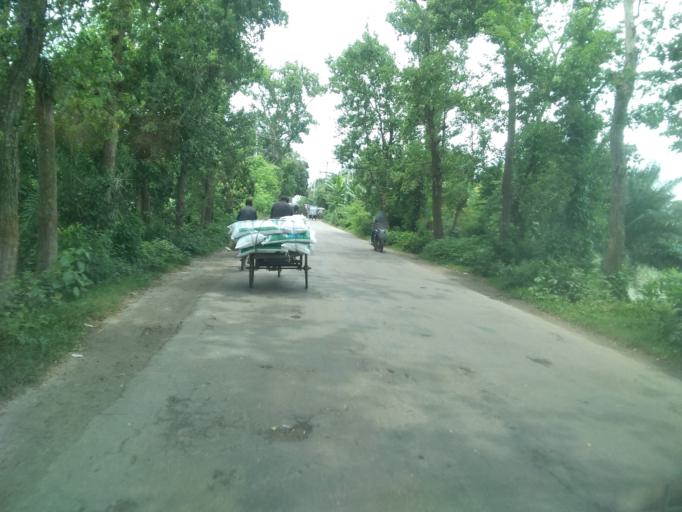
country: IN
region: West Bengal
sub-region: North 24 Parganas
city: Taki
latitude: 22.5753
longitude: 88.9993
